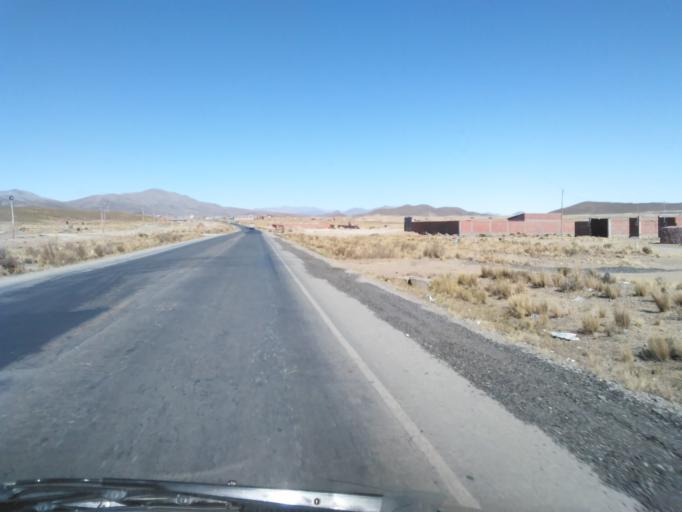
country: BO
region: Oruro
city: Oruro
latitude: -18.0055
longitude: -67.0403
